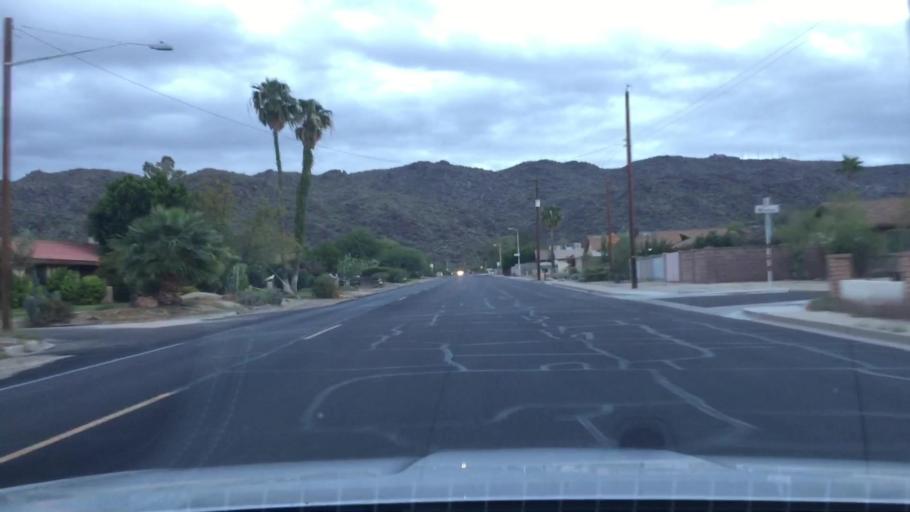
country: US
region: Arizona
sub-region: Maricopa County
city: Phoenix
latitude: 33.3695
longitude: -112.0488
